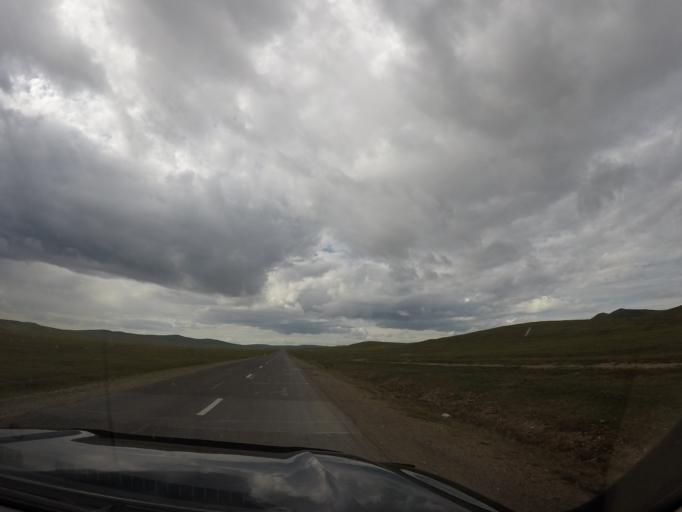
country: MN
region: Hentiy
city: Avraga
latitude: 47.4969
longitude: 109.4488
